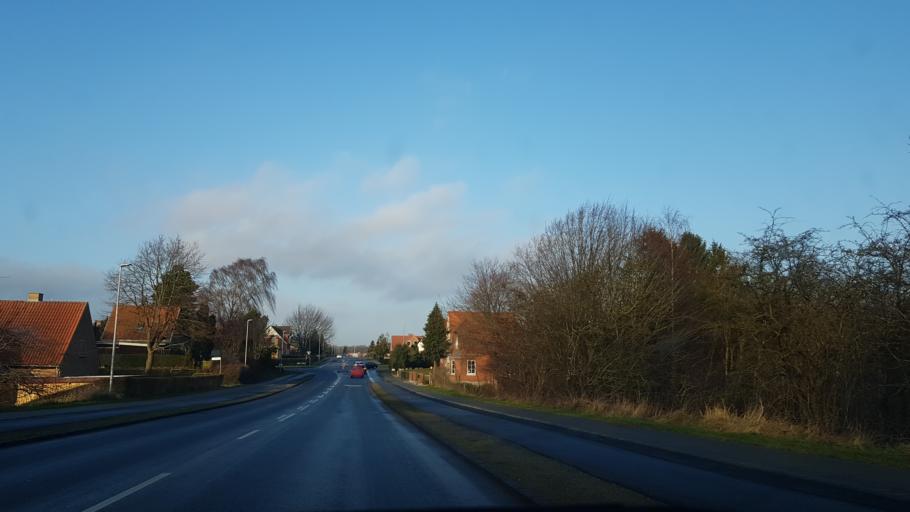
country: DK
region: South Denmark
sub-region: Haderslev Kommune
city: Haderslev
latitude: 55.2410
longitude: 9.4997
